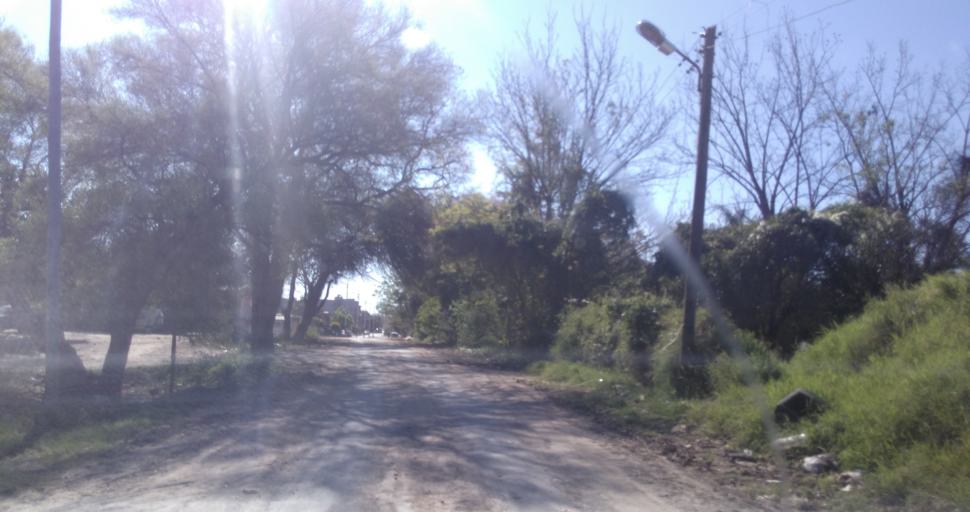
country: AR
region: Chaco
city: Resistencia
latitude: -27.4453
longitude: -58.9643
